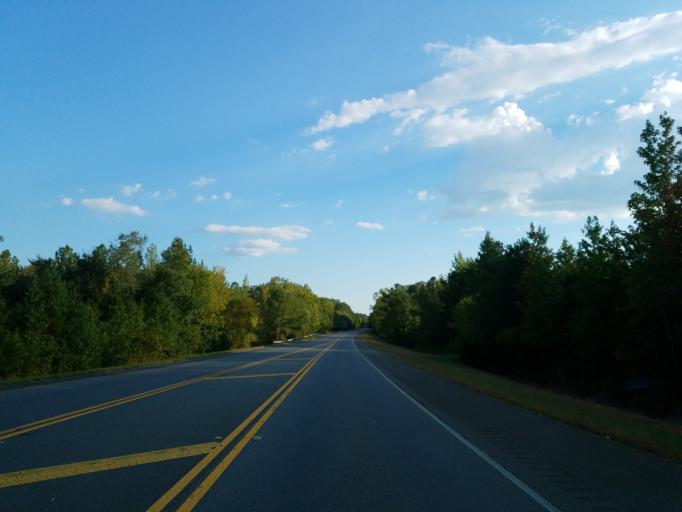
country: US
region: Georgia
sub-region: Murray County
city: Chatsworth
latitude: 34.6661
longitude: -84.7215
